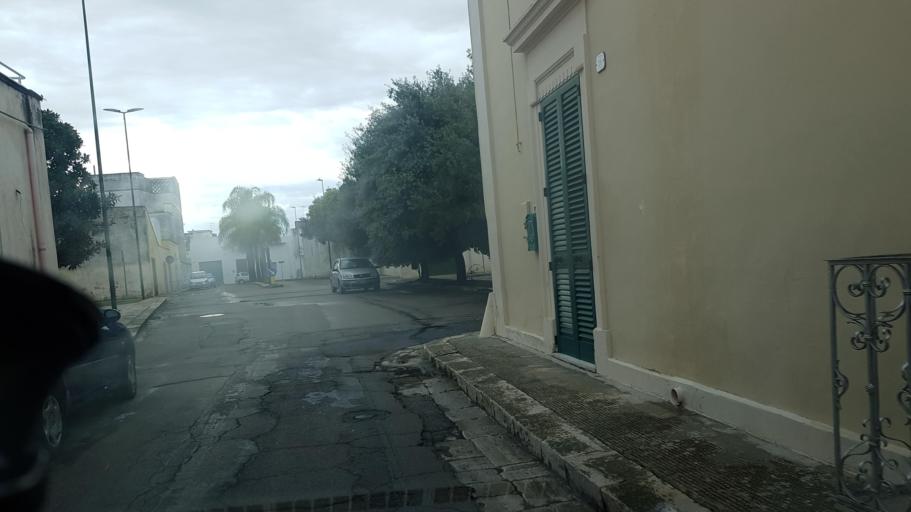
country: IT
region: Apulia
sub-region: Provincia di Lecce
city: Guagnano
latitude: 40.4005
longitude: 17.9517
